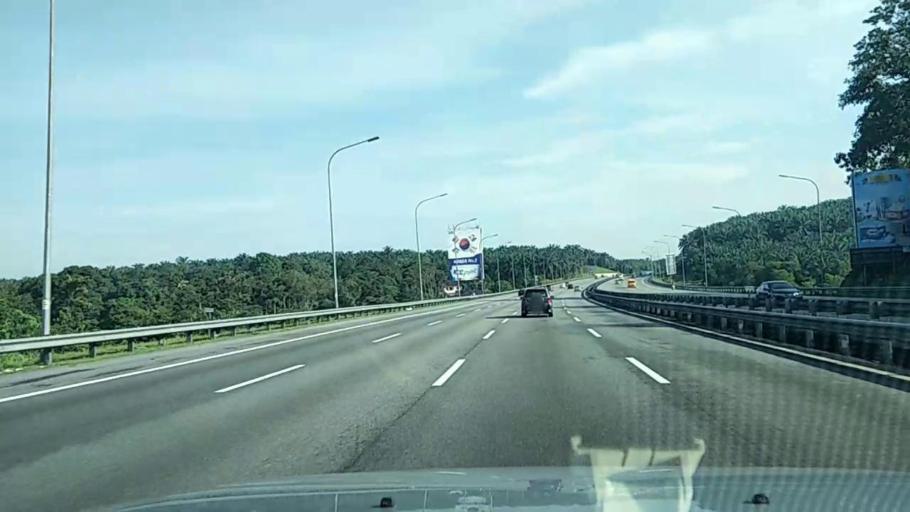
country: MY
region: Negeri Sembilan
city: Kampung Baharu Nilai
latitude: 2.7810
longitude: 101.8124
